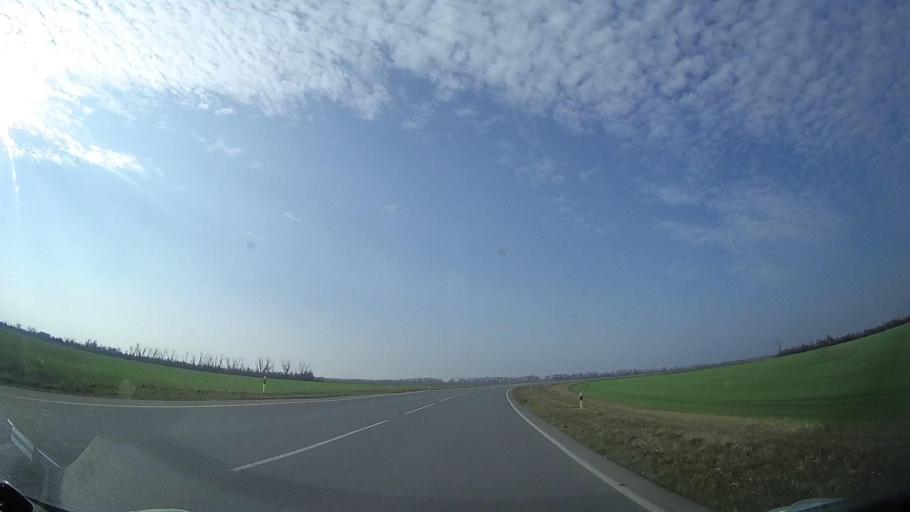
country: RU
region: Rostov
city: Tselina
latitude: 46.5144
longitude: 41.0696
